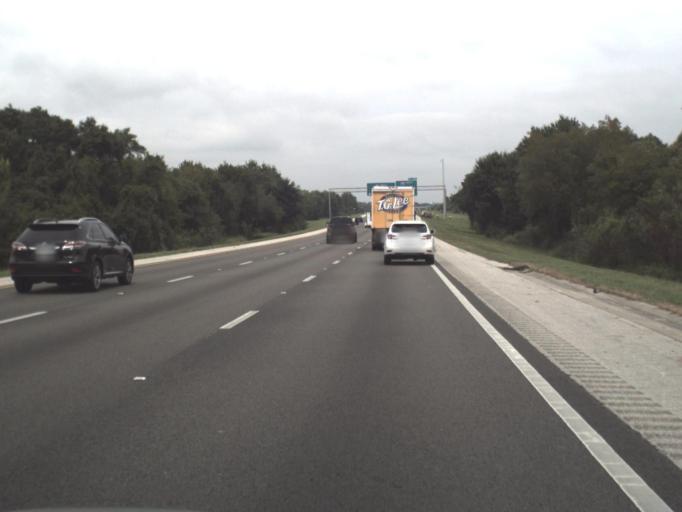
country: US
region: Florida
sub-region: Manatee County
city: Ellenton
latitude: 27.5602
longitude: -82.5120
